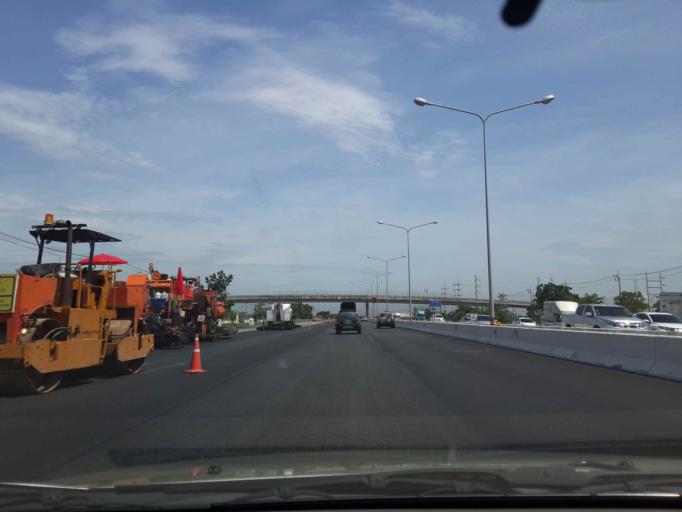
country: TH
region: Samut Prakan
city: Ban Khlong Bang Sao Thong
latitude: 13.6484
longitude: 100.8774
